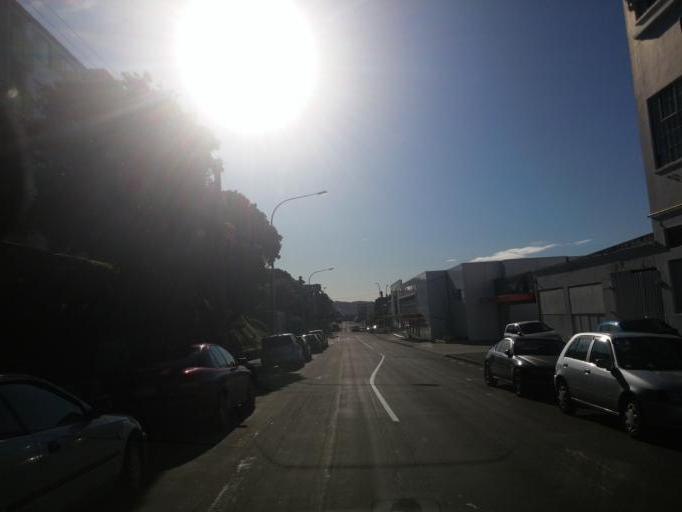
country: NZ
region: Wellington
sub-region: Wellington City
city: Wellington
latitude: -41.3081
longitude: 174.7765
